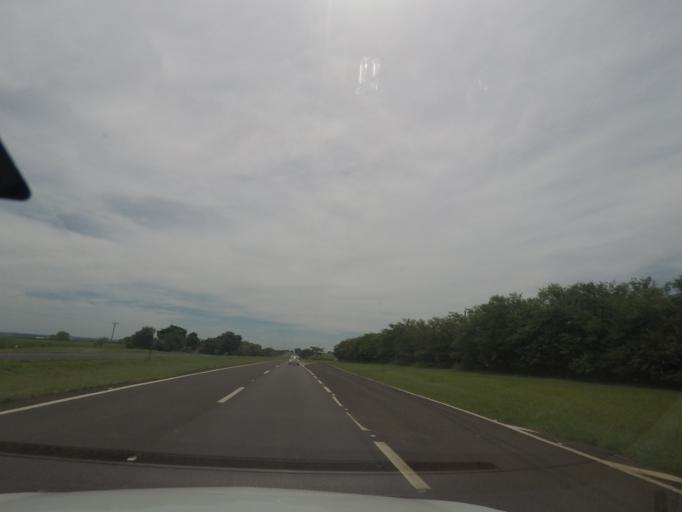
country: BR
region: Sao Paulo
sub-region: Bebedouro
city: Bebedouro
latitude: -20.9650
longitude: -48.4419
